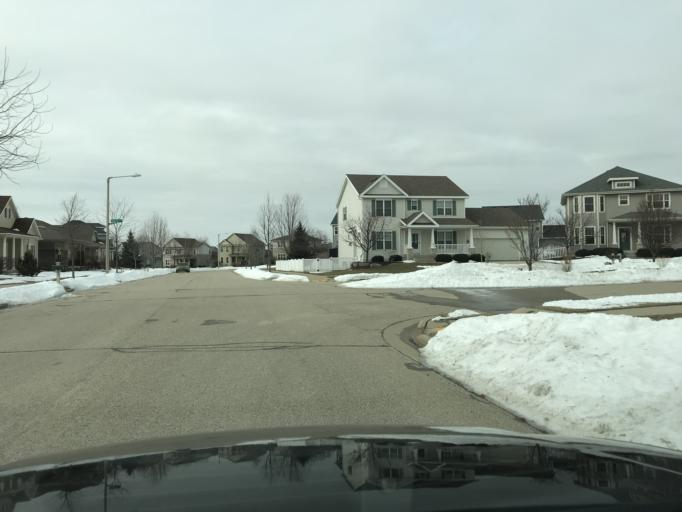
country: US
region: Wisconsin
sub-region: Dane County
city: Monona
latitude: 43.0896
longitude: -89.2720
